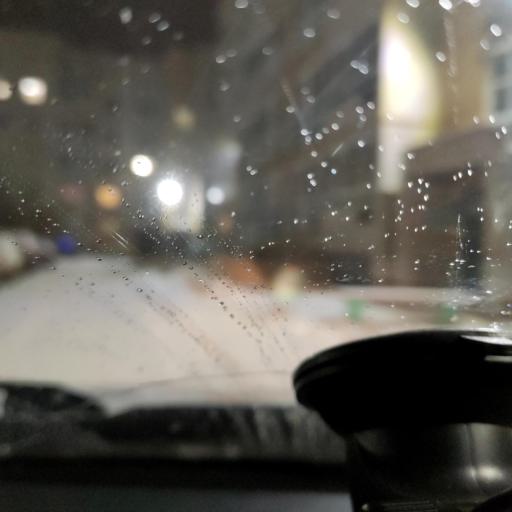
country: RU
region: Perm
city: Gamovo
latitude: 57.8722
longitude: 56.0956
